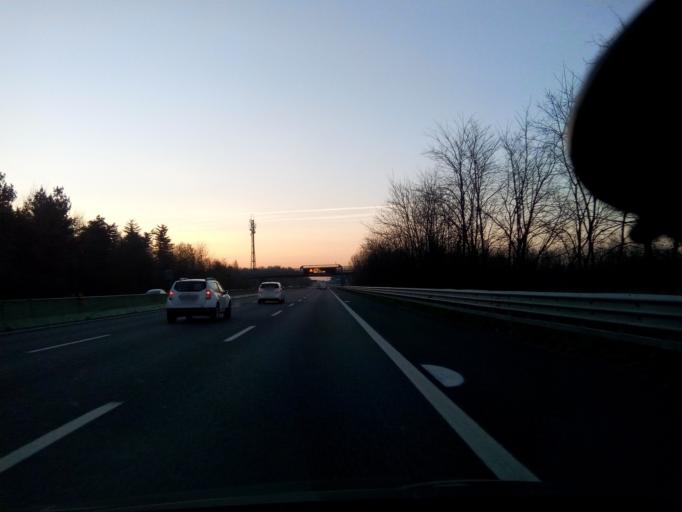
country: IT
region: Lombardy
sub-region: Citta metropolitana di Milano
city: Cantalupo
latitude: 45.5846
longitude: 8.9889
